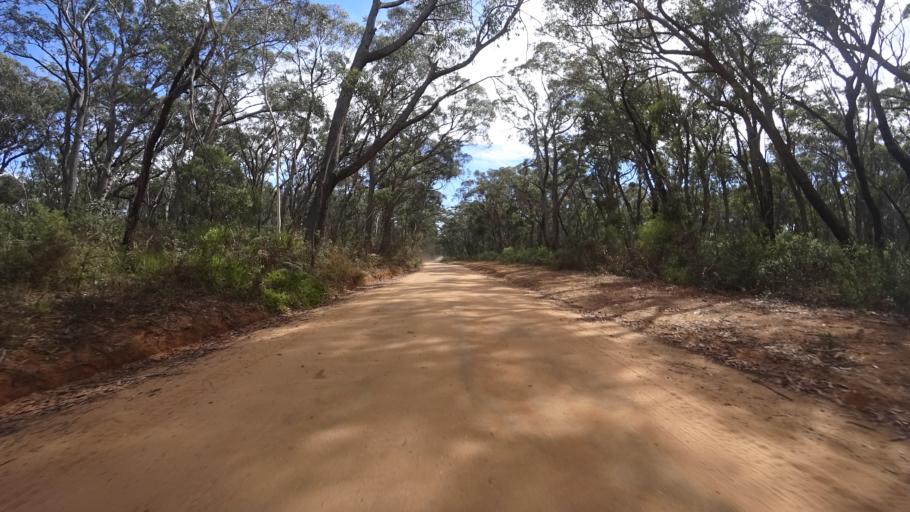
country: AU
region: New South Wales
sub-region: Lithgow
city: Lithgow
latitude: -33.3132
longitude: 150.2396
